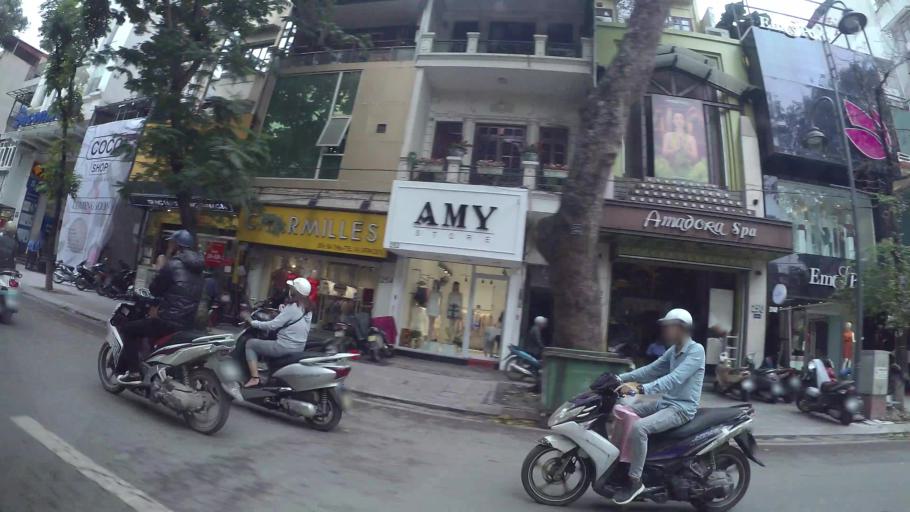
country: VN
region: Ha Noi
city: Hai BaTrung
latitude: 21.0140
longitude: 105.8491
